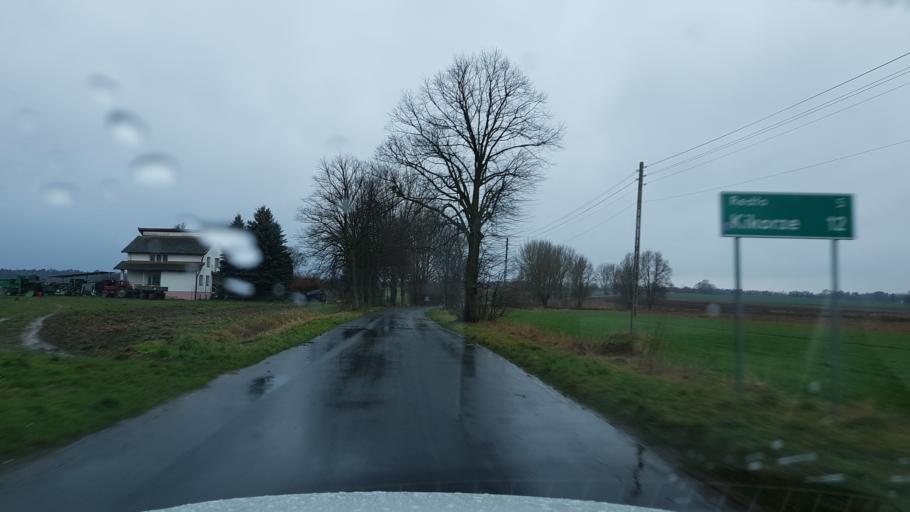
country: PL
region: West Pomeranian Voivodeship
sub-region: Powiat goleniowski
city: Nowogard
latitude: 53.5782
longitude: 15.1324
